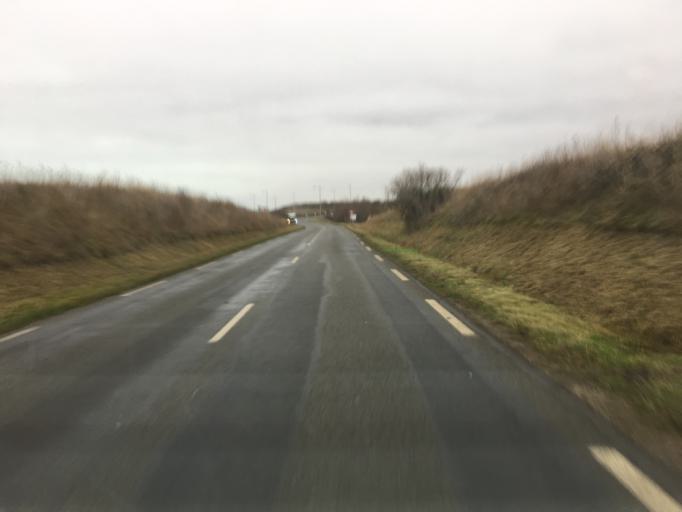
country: FR
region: Nord-Pas-de-Calais
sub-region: Departement du Pas-de-Calais
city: Equihen-Plage
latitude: 50.6884
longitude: 1.5763
